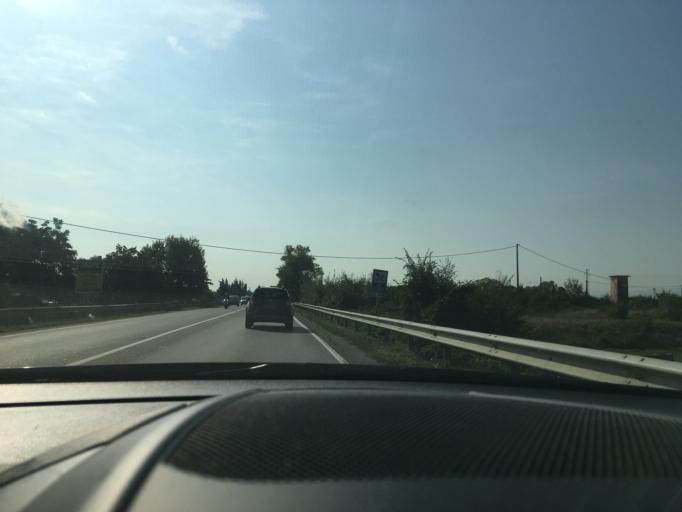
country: IT
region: Emilia-Romagna
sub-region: Provincia di Rimini
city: Bellaria-Igea Marina
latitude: 44.1080
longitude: 12.4846
